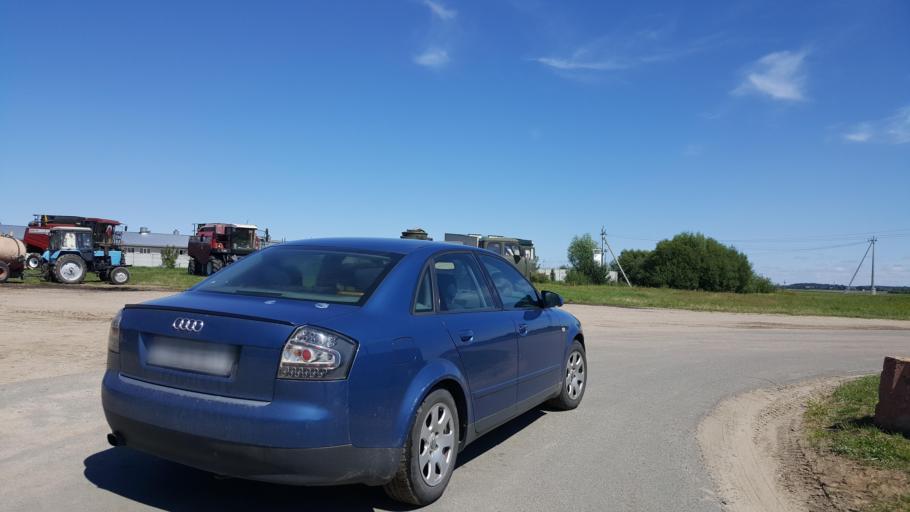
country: BY
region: Brest
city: Charnawchytsy
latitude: 52.2175
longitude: 23.7468
